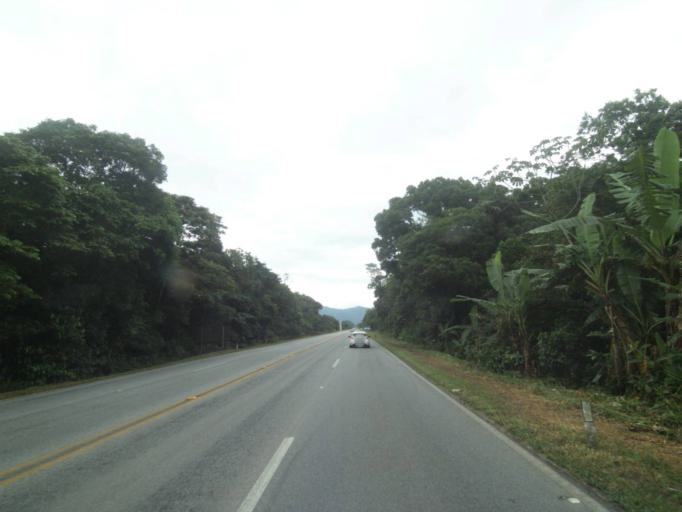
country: BR
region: Parana
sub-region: Guaratuba
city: Guaratuba
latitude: -25.7967
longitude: -48.5583
